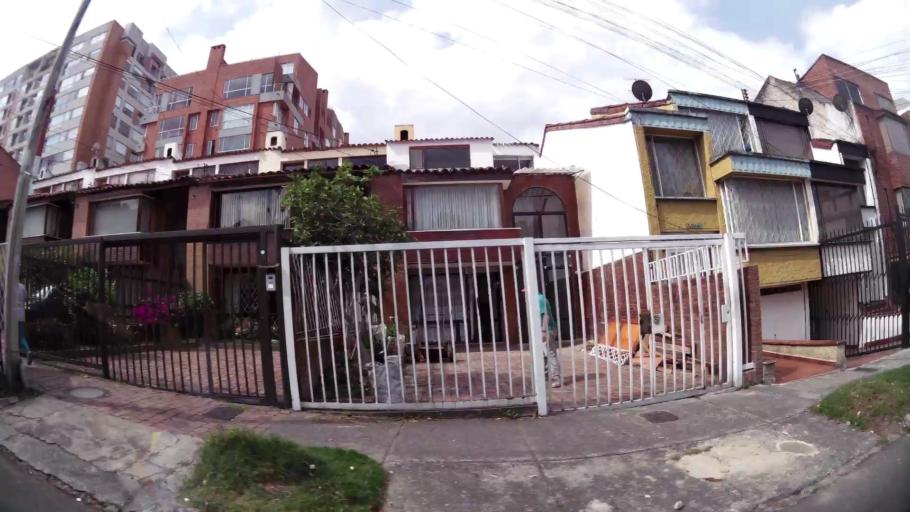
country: CO
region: Bogota D.C.
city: Barrio San Luis
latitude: 4.7247
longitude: -74.0285
